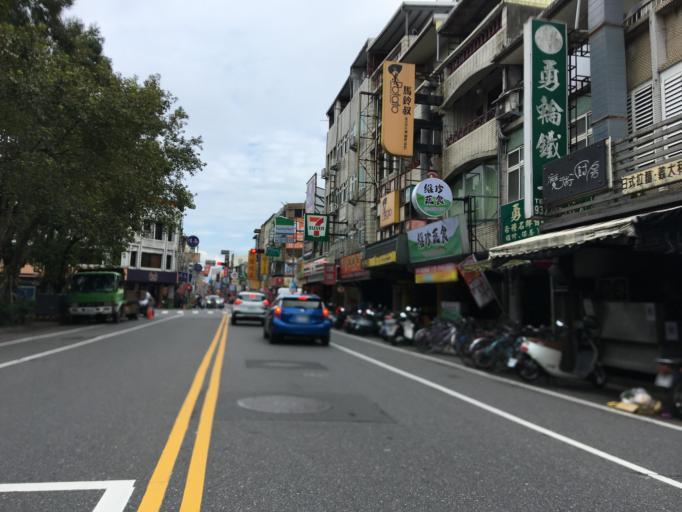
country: TW
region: Taiwan
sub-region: Yilan
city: Yilan
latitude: 24.7464
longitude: 121.7491
